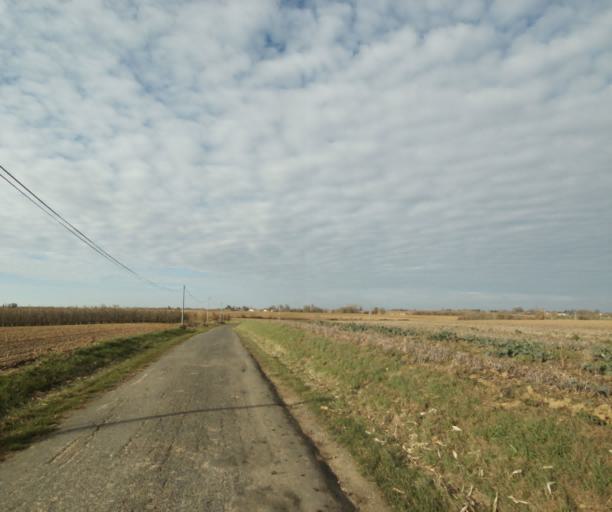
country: FR
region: Poitou-Charentes
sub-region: Departement de la Charente-Maritime
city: Corme-Royal
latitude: 45.7294
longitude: -0.7928
